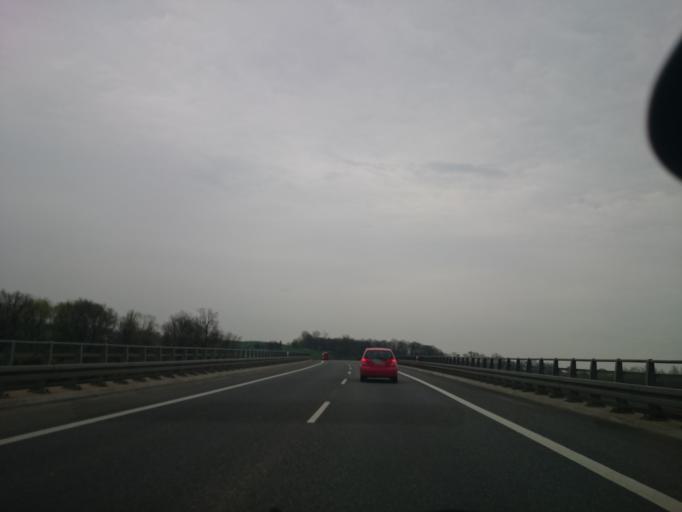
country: PL
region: Opole Voivodeship
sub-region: Powiat nyski
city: Otmuchow
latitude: 50.4572
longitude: 17.1890
